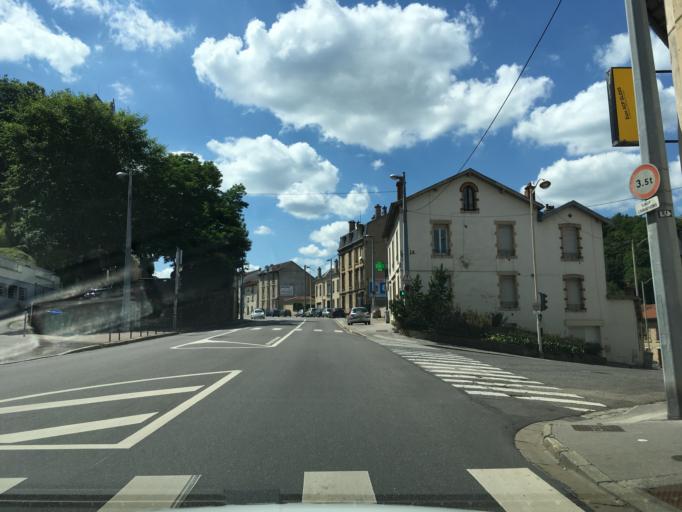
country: FR
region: Lorraine
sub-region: Departement de Meurthe-et-Moselle
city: Laxou
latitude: 48.6973
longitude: 6.1566
